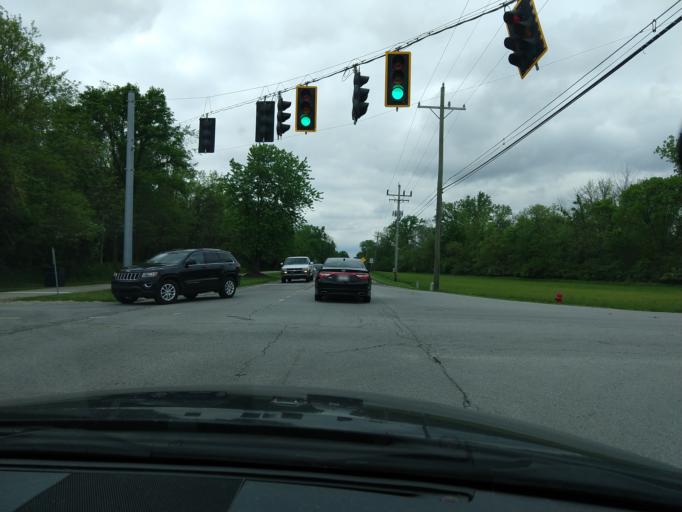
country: US
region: Indiana
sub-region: Hamilton County
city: Westfield
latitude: 40.0219
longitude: -86.1275
